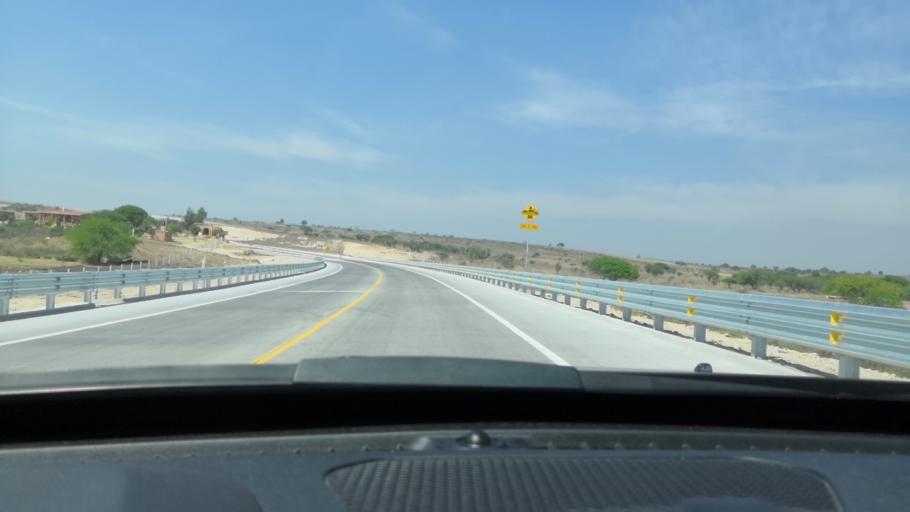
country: MX
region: Guanajuato
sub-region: Purisima del Rincon
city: Potrerillos (Guanajal)
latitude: 21.0865
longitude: -101.8519
